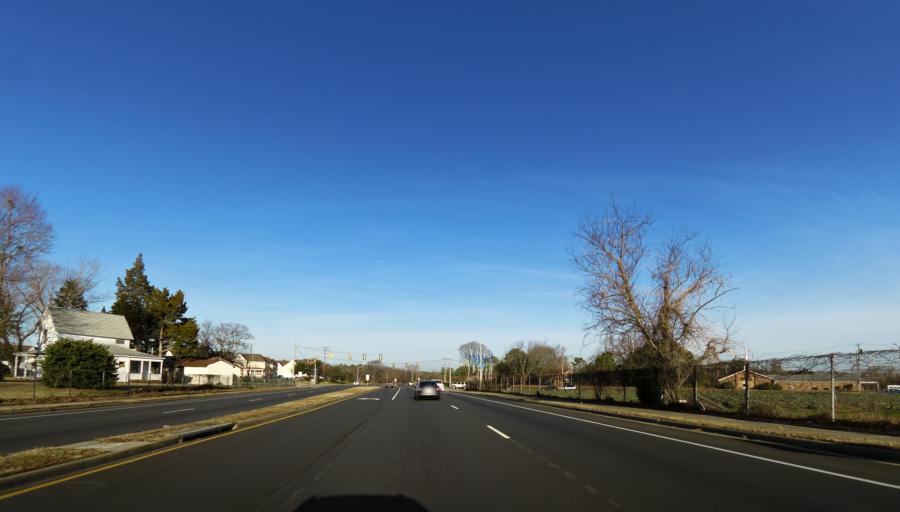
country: US
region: Virginia
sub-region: City of Hampton
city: Hampton
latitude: 37.0250
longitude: -76.3880
